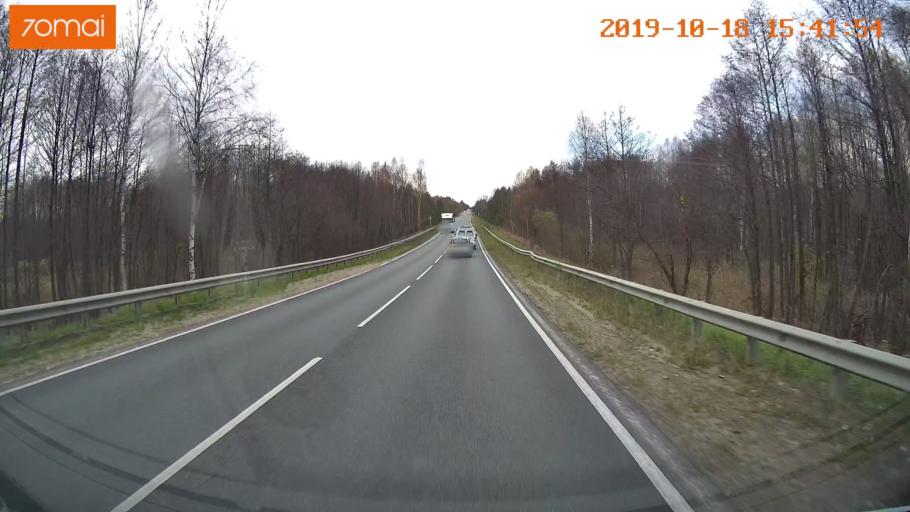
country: RU
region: Vladimir
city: Golovino
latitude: 55.9504
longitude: 40.5757
